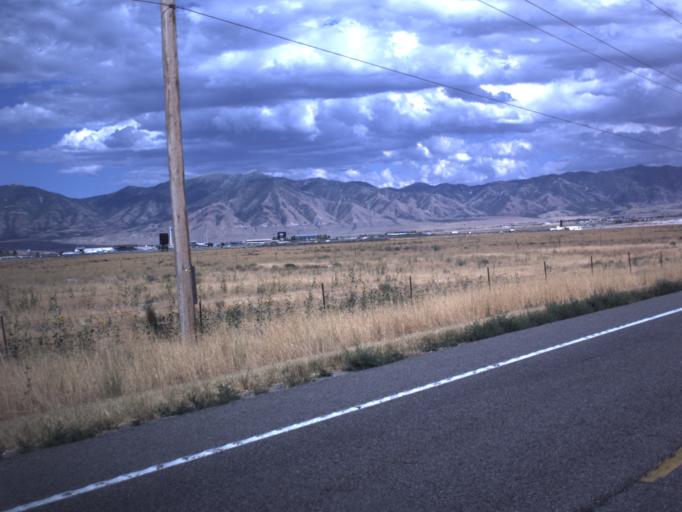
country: US
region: Utah
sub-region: Tooele County
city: Grantsville
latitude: 40.5798
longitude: -112.3965
